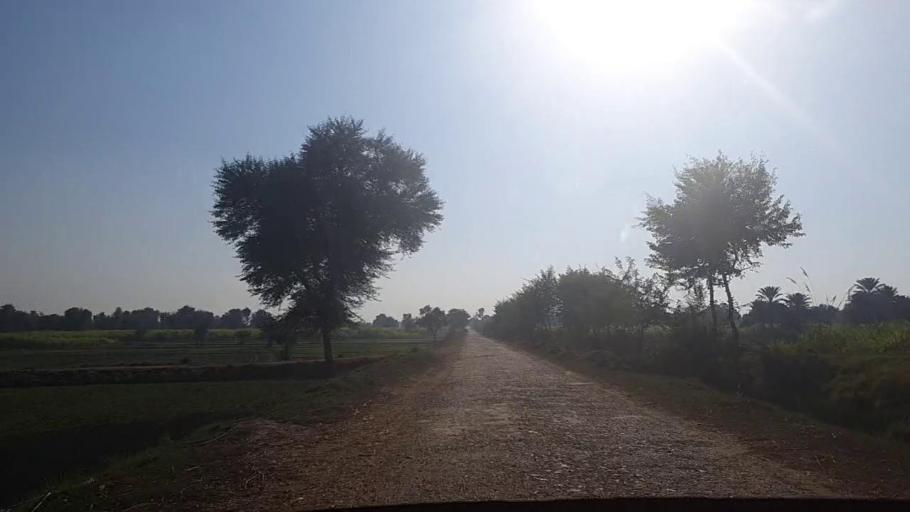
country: PK
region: Sindh
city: Gambat
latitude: 27.3708
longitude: 68.4636
